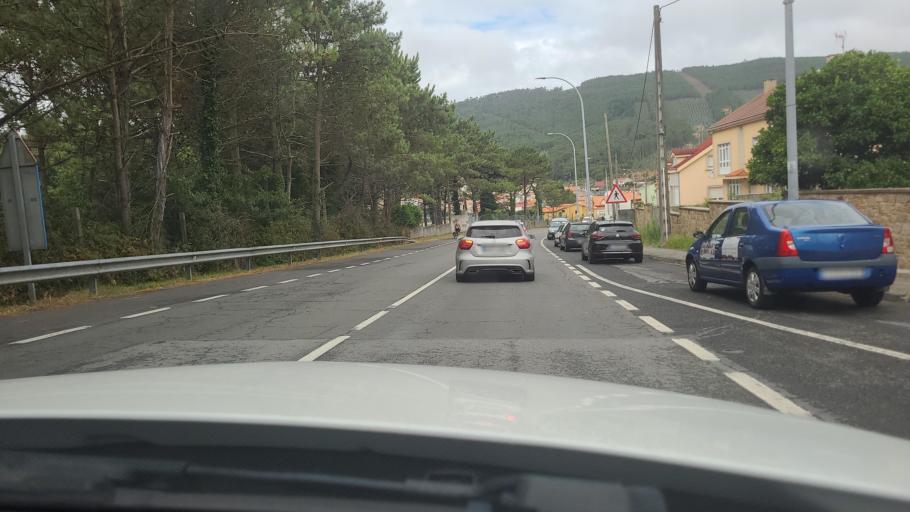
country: ES
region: Galicia
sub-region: Provincia da Coruna
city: Corcubion
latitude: 42.9431
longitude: -9.2268
